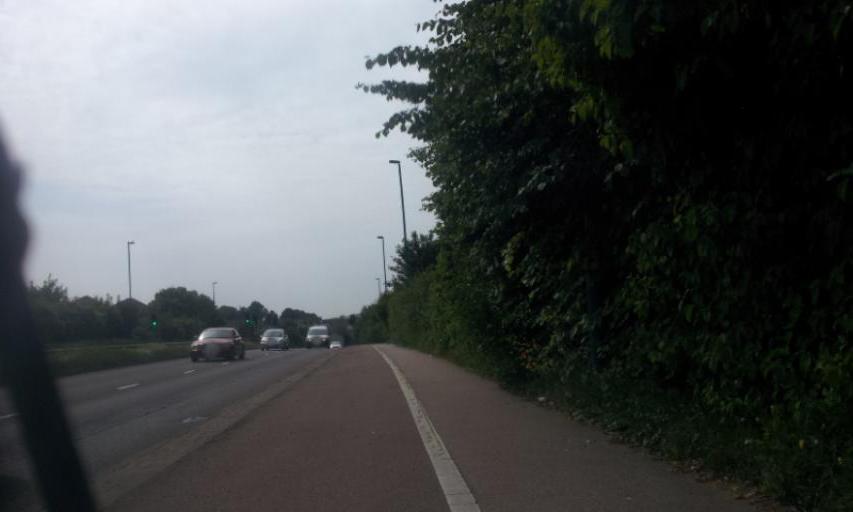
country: GB
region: England
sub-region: Kent
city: Gillingham
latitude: 51.3907
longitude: 0.5744
